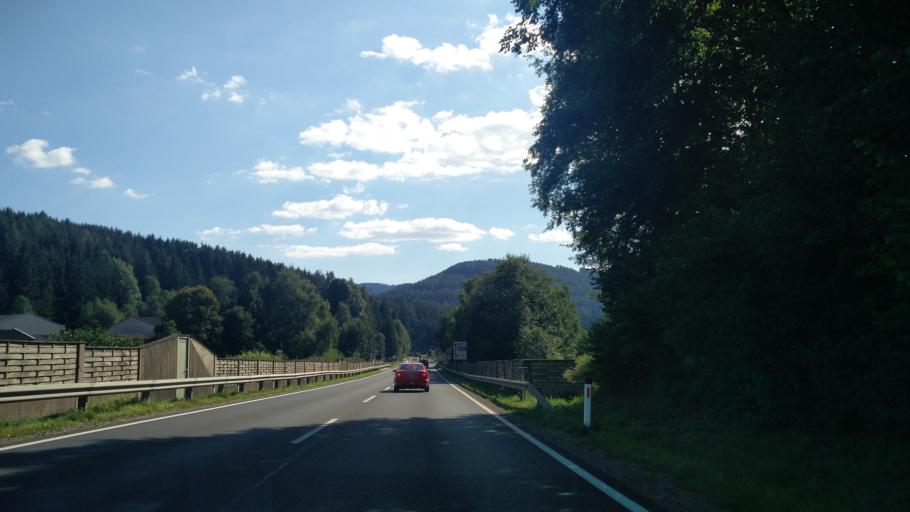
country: AT
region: Styria
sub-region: Politischer Bezirk Leoben
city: Trofaiach
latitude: 47.4061
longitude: 14.9982
